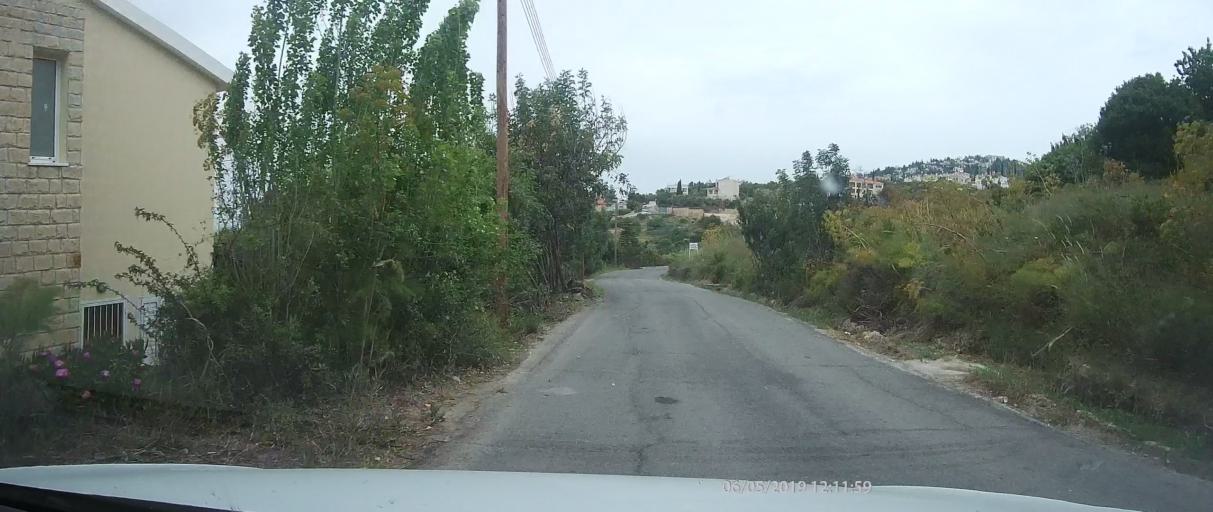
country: CY
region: Pafos
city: Tala
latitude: 34.8393
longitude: 32.4287
